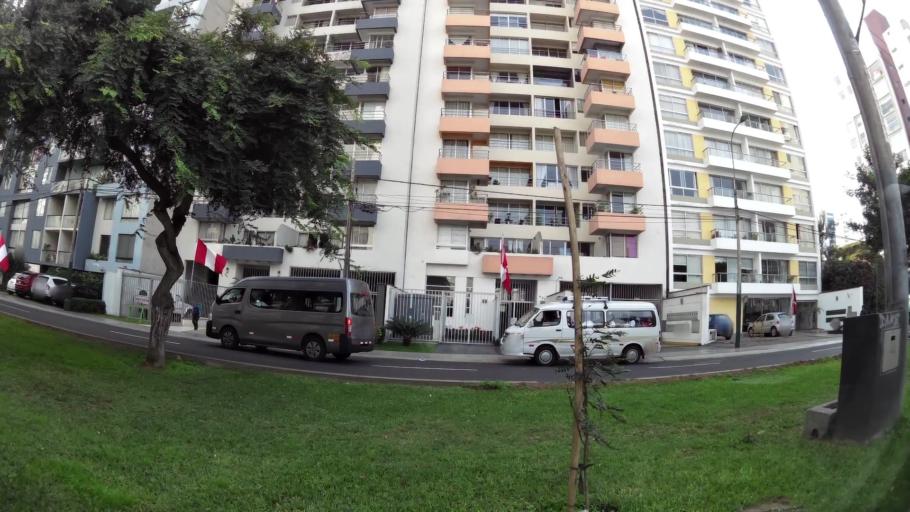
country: PE
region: Lima
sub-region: Lima
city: San Isidro
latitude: -12.0914
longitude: -77.0586
